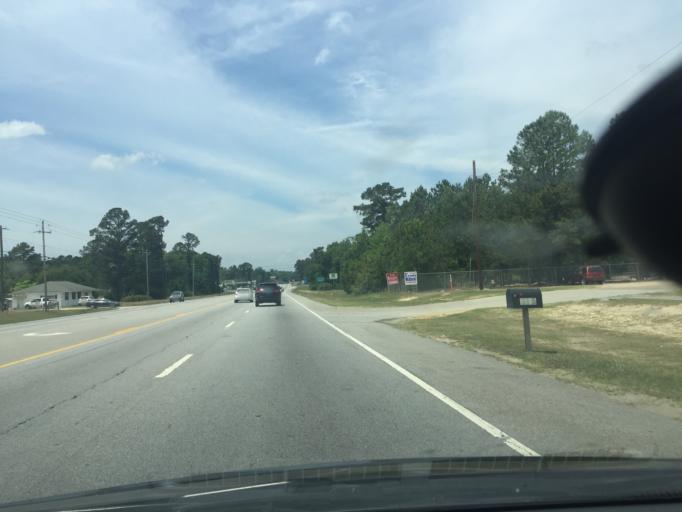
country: US
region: Georgia
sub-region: Chatham County
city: Bloomingdale
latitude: 32.1418
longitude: -81.3280
